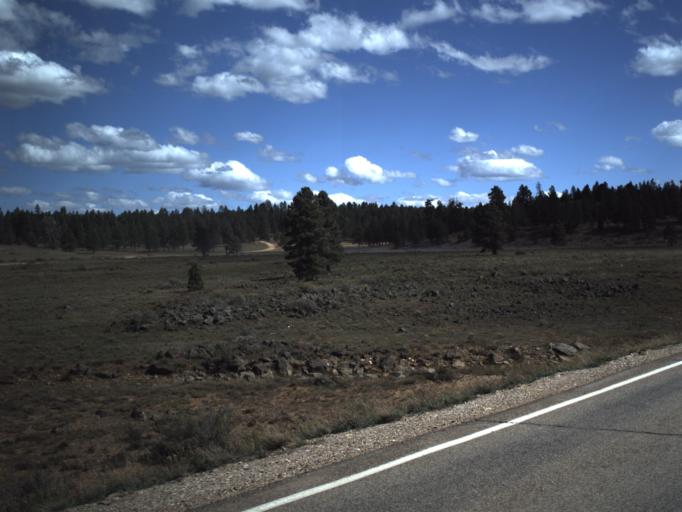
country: US
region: Utah
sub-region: Garfield County
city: Panguitch
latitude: 37.5060
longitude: -112.6264
